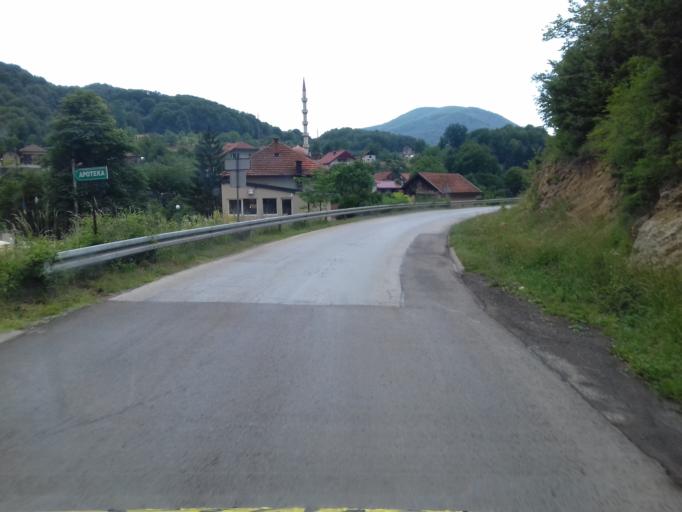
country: BA
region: Federation of Bosnia and Herzegovina
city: Visoko
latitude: 43.9644
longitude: 18.1820
